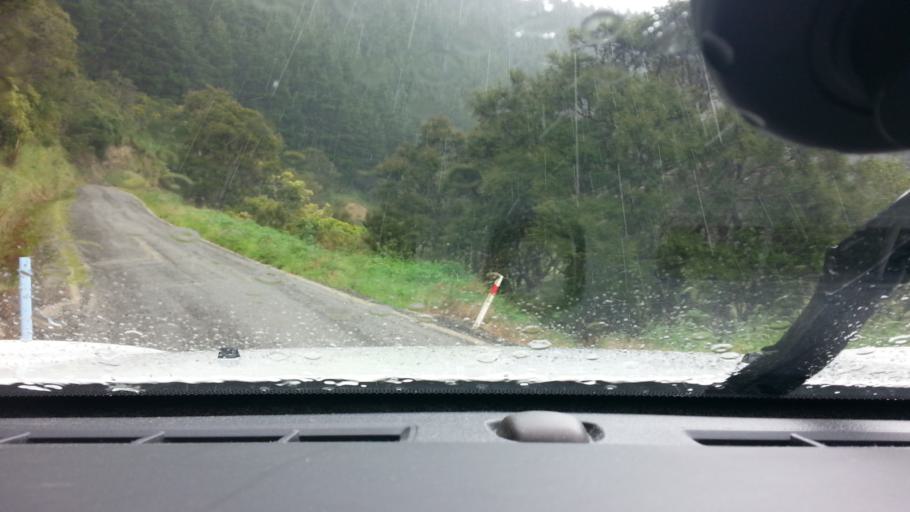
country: NZ
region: Wellington
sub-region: Masterton District
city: Masterton
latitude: -40.9352
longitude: 175.5089
